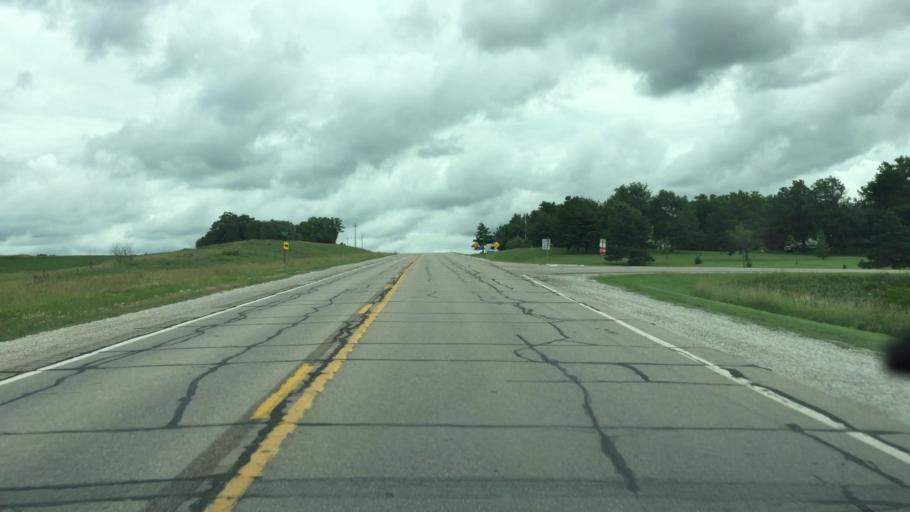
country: US
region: Iowa
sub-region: Jasper County
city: Monroe
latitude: 41.5430
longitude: -93.0985
